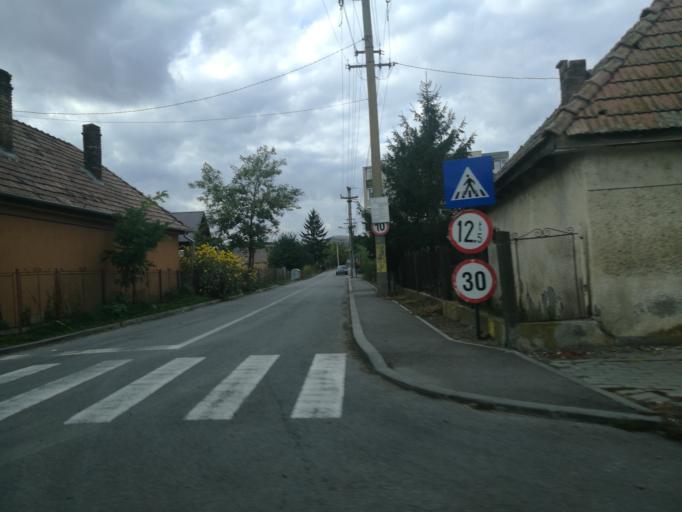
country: RO
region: Mures
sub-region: Comuna Ungheni
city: Ungheni
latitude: 46.4874
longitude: 24.4618
